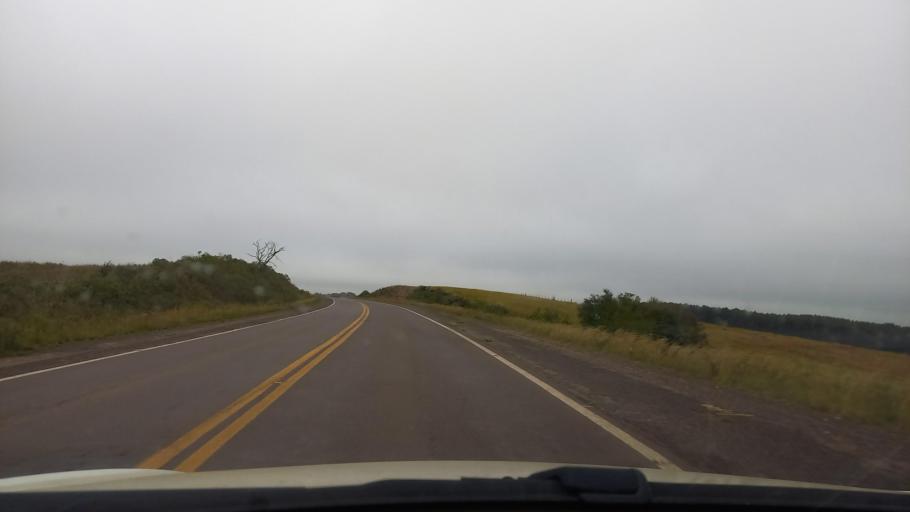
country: BR
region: Rio Grande do Sul
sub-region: Rosario Do Sul
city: Rosario do Sul
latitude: -30.1460
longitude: -54.6752
